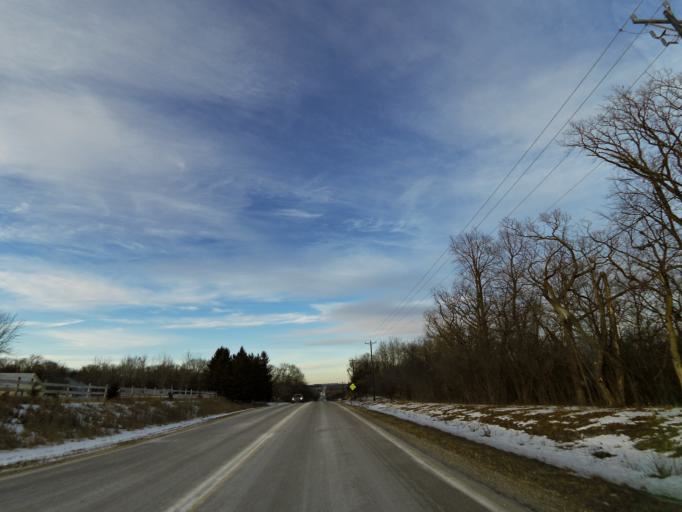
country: US
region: Minnesota
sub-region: Washington County
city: Afton
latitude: 44.8968
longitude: -92.8429
